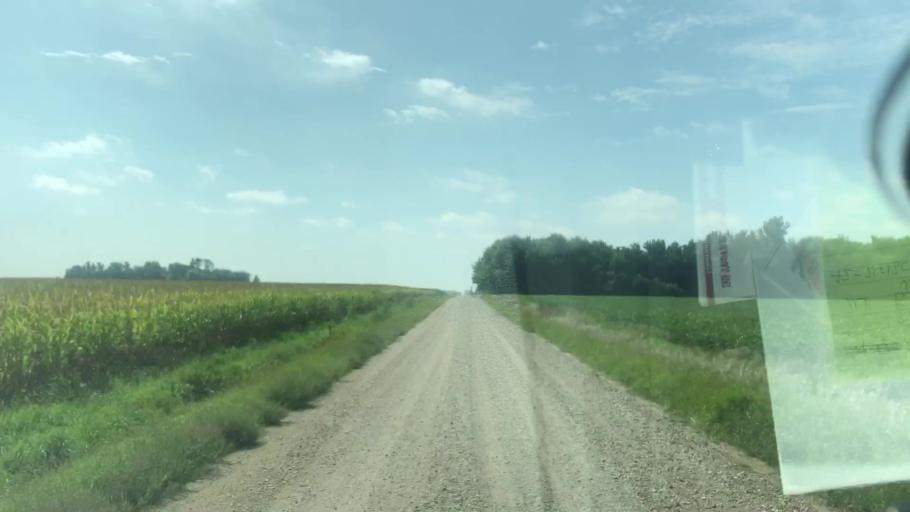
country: US
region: Iowa
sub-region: O'Brien County
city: Sheldon
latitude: 43.1941
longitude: -95.9416
